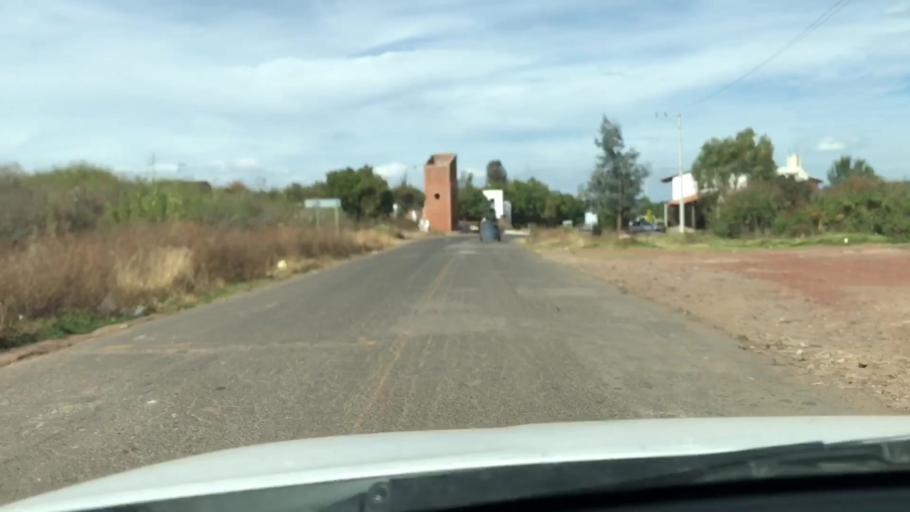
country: MX
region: Jalisco
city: Chiquilistlan
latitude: 20.1378
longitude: -103.7173
